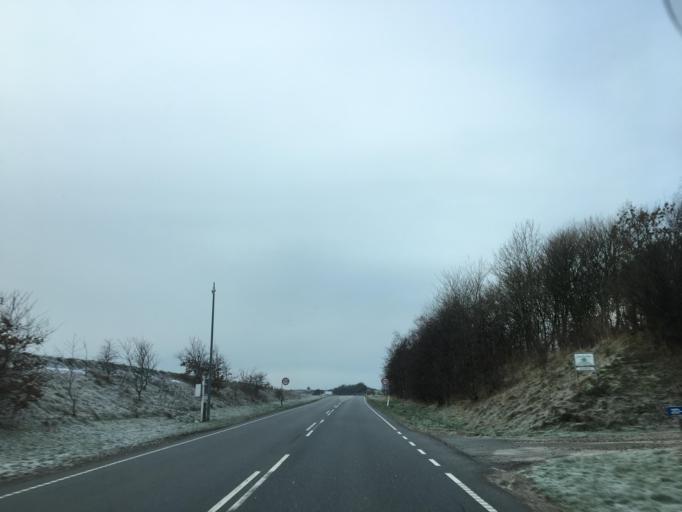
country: DK
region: North Denmark
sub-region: Thisted Kommune
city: Hurup
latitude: 56.7591
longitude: 8.4296
